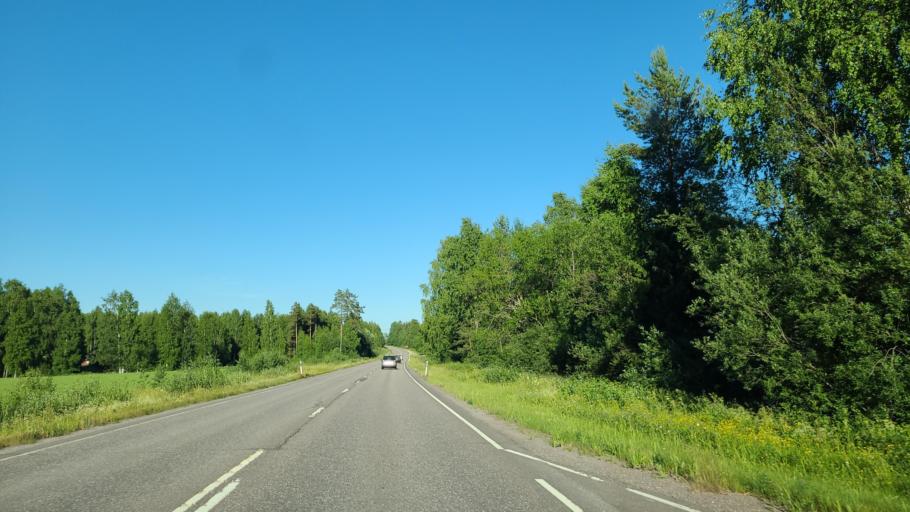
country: FI
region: Southern Savonia
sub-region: Pieksaemaeki
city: Jaeppilae
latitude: 62.2890
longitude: 27.5371
